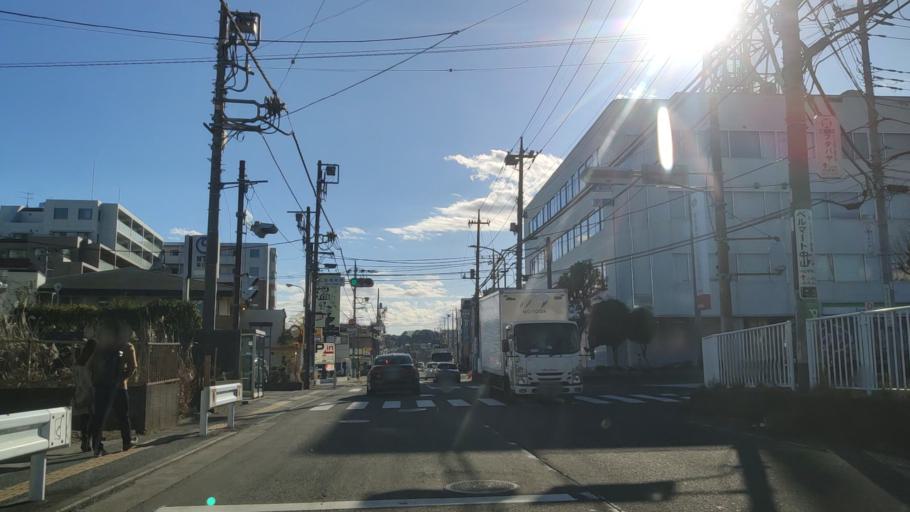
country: JP
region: Tokyo
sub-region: Machida-shi
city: Machida
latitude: 35.5160
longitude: 139.5430
